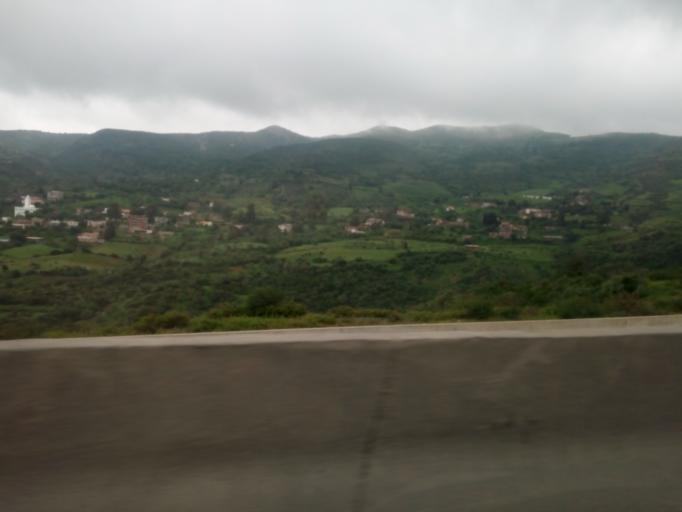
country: DZ
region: Bouira
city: Lakhdaria
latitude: 36.5906
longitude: 3.4899
